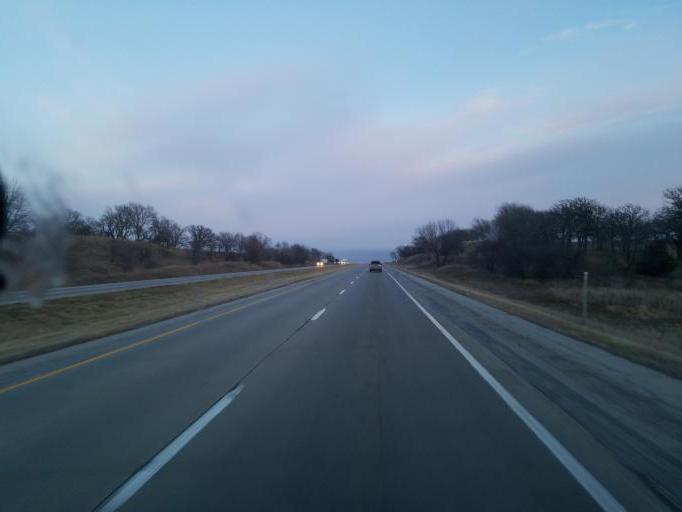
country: US
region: Iowa
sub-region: Pottawattamie County
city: Avoca
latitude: 41.4982
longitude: -95.3053
